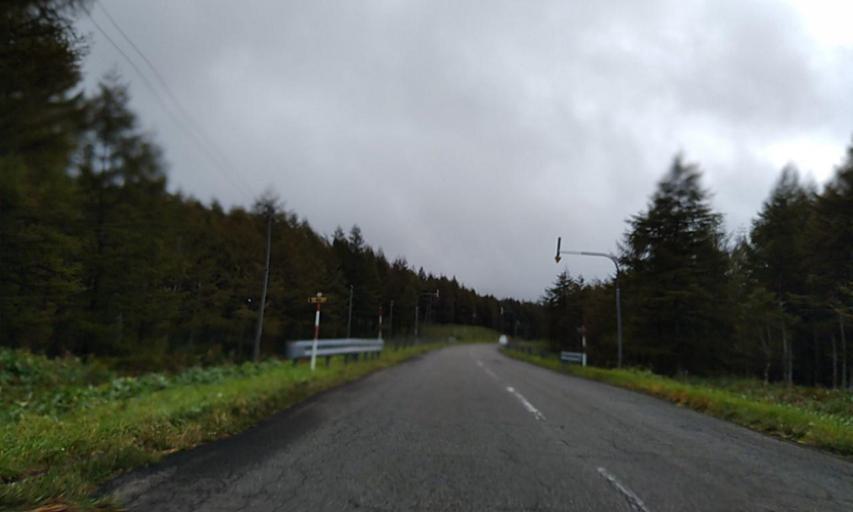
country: JP
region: Hokkaido
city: Shibetsu
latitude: 43.6089
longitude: 144.6051
